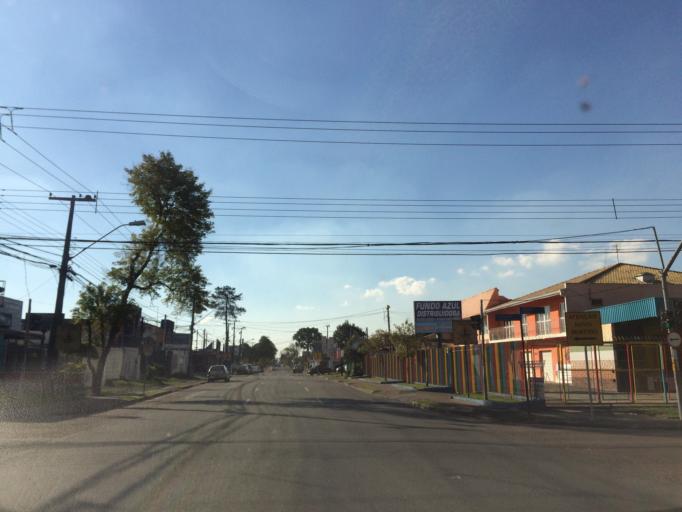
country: BR
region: Parana
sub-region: Sao Jose Dos Pinhais
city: Sao Jose dos Pinhais
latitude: -25.4990
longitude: -49.2374
